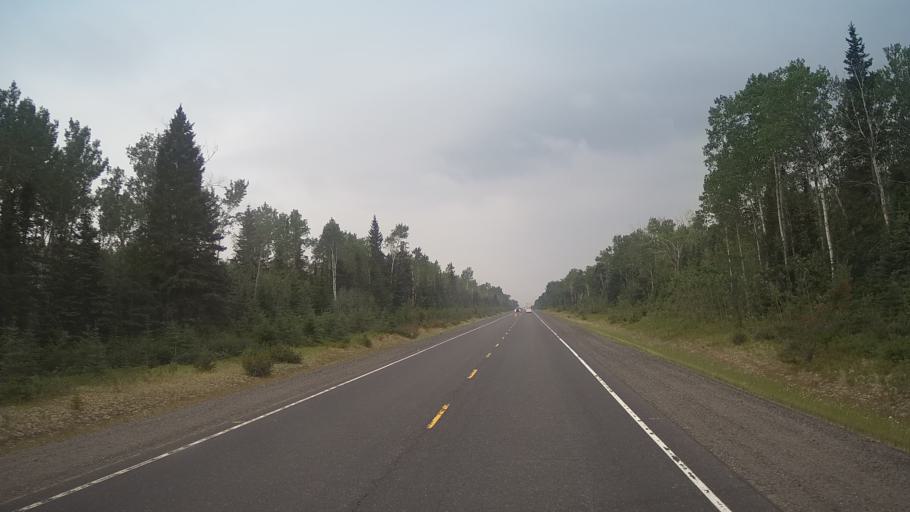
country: CA
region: Ontario
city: Greenstone
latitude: 49.2229
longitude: -88.1930
